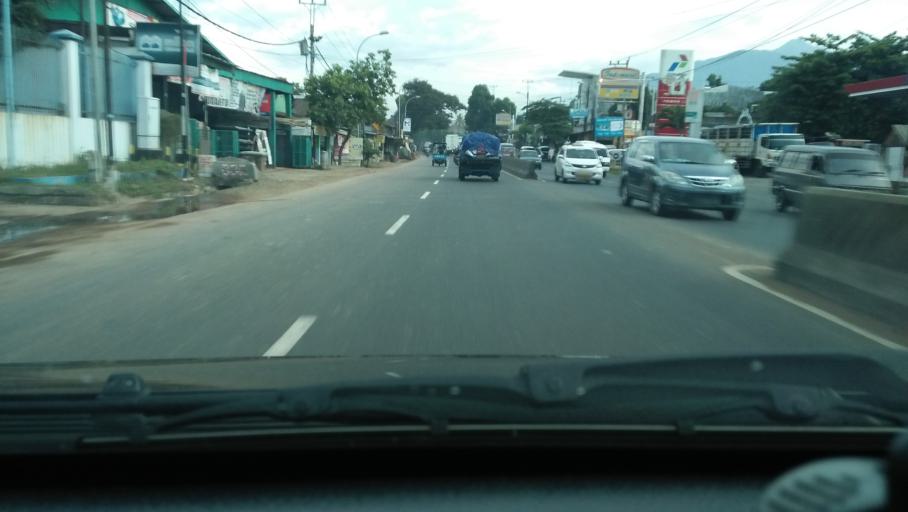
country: ID
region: Central Java
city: Ungaran
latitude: -7.0994
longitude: 110.4094
